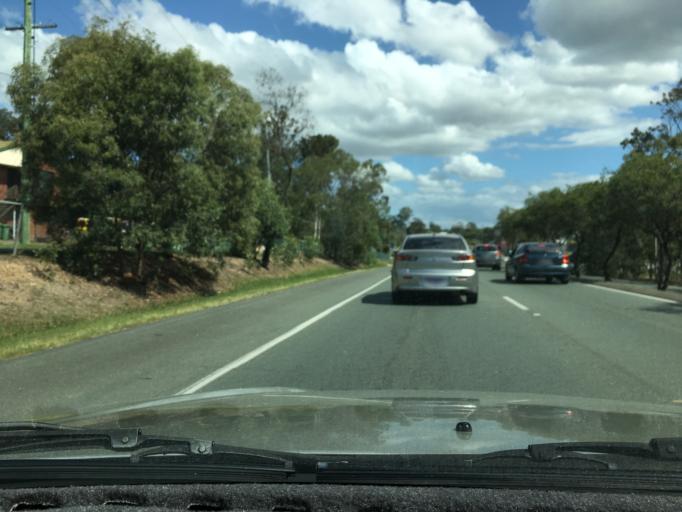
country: AU
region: Queensland
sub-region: Logan
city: Waterford West
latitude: -27.6727
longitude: 153.1222
